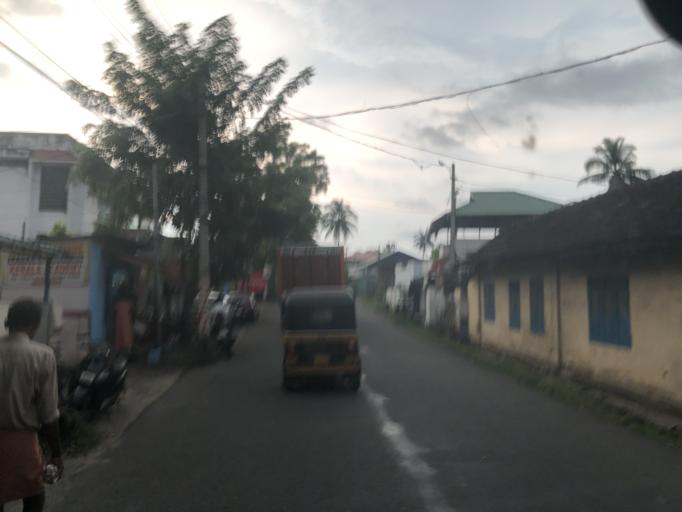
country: IN
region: Kerala
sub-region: Ernakulam
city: Cochin
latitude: 9.9522
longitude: 76.2475
